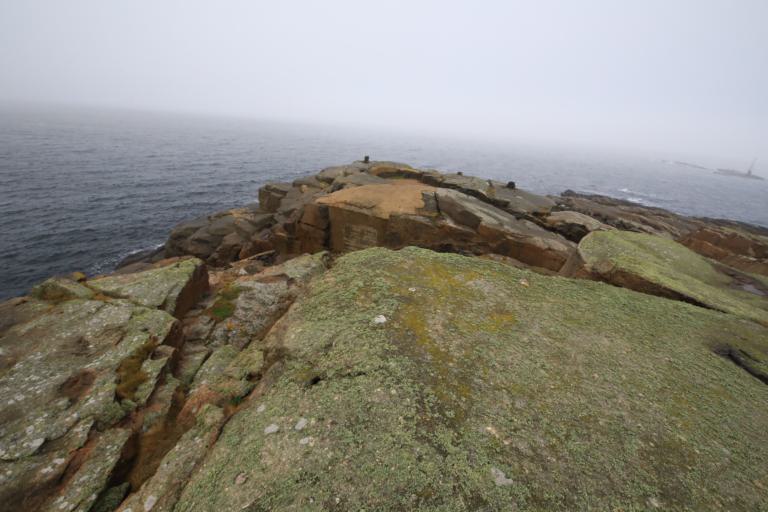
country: SE
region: Vaestra Goetaland
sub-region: Ockero Kommun
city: Hono
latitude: 57.6344
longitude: 11.5964
